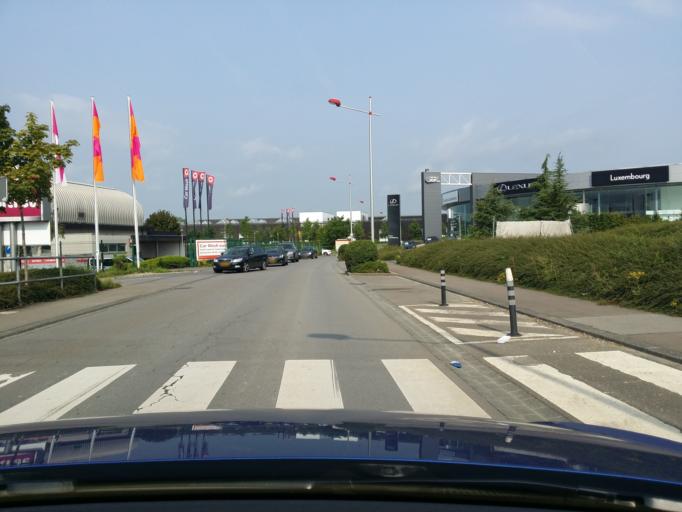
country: LU
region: Luxembourg
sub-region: Canton de Luxembourg
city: Strassen
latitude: 49.6083
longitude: 6.0775
